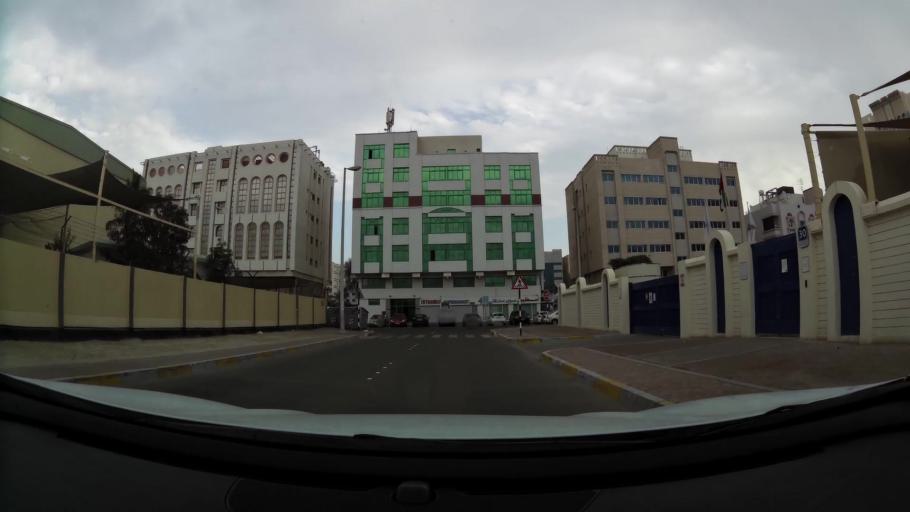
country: AE
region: Abu Dhabi
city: Abu Dhabi
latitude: 24.4756
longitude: 54.3762
